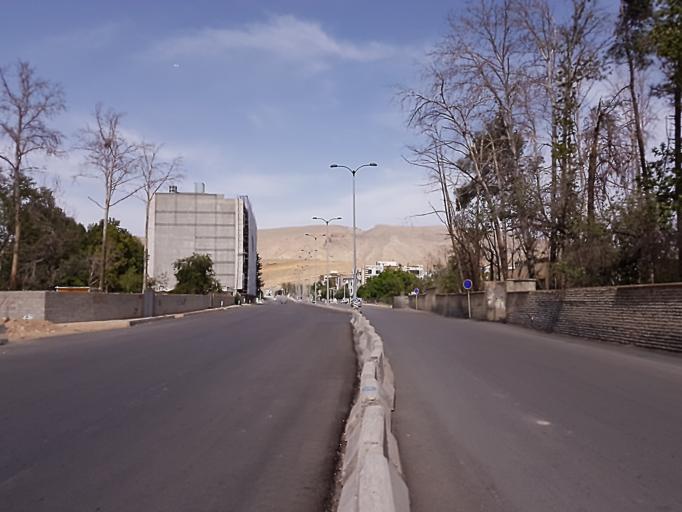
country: IR
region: Fars
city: Shiraz
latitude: 29.6543
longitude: 52.4856
